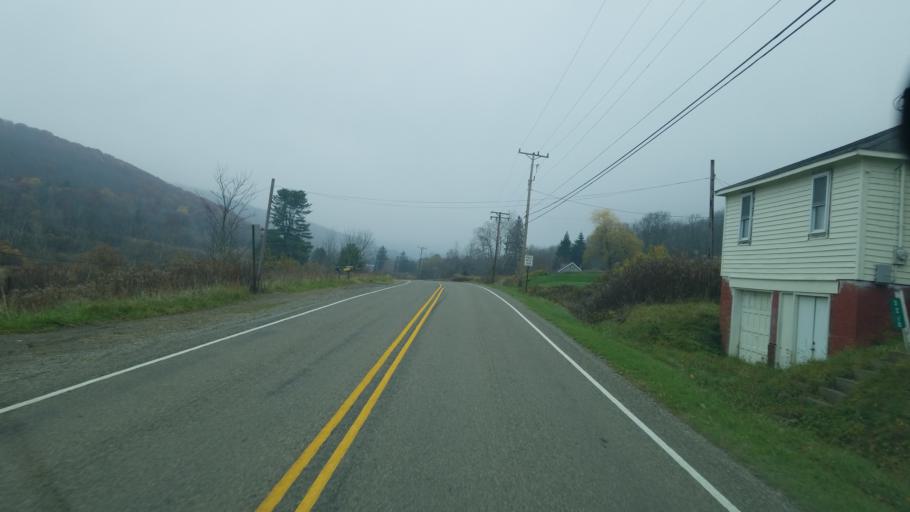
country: US
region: Pennsylvania
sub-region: McKean County
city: Smethport
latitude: 41.8817
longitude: -78.4924
